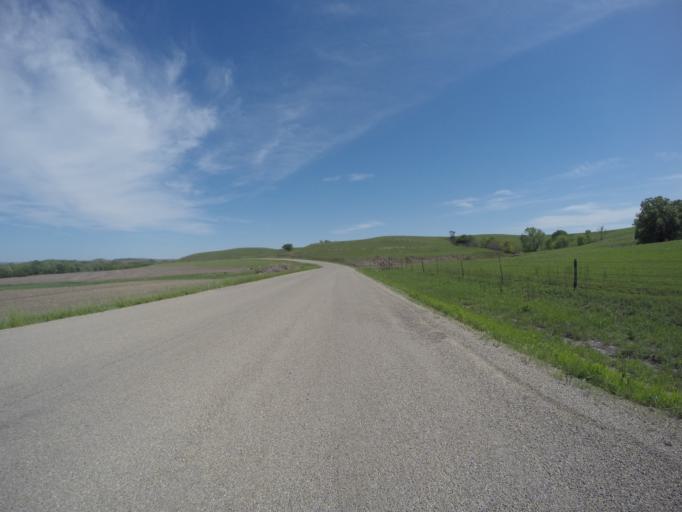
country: US
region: Kansas
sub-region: Riley County
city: Ogden
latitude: 39.0325
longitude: -96.6210
